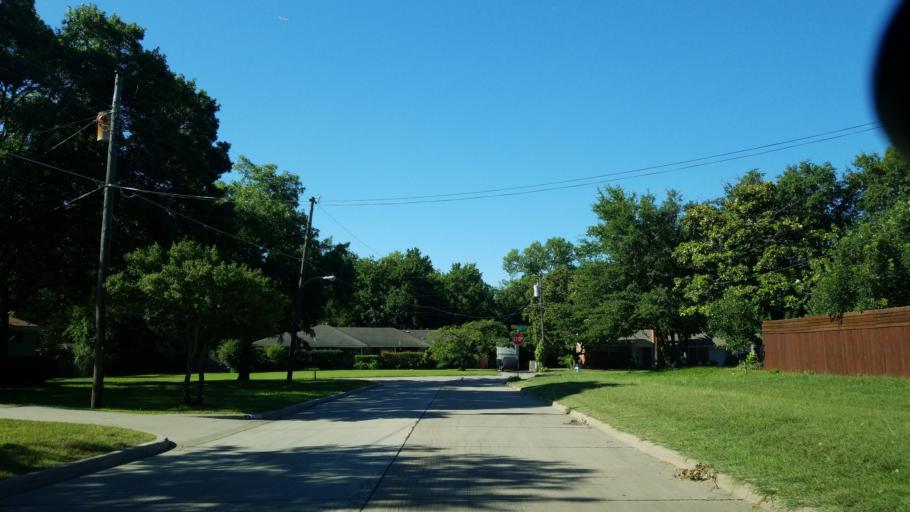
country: US
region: Texas
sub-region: Dallas County
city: Carrollton
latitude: 32.9512
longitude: -96.9003
